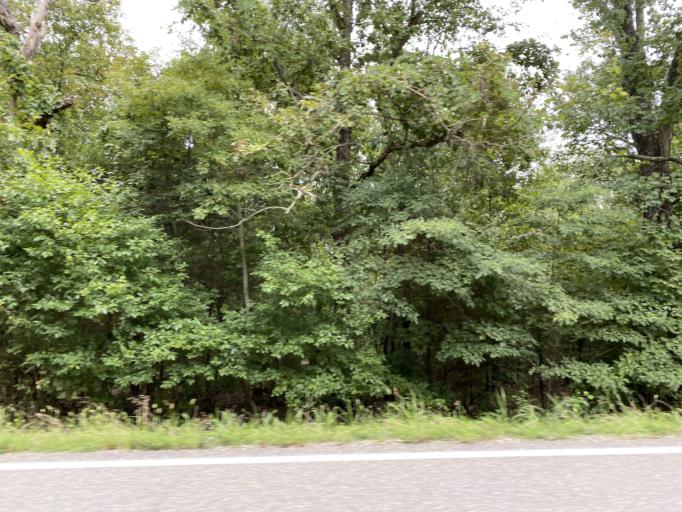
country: US
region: Arkansas
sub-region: Fulton County
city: Salem
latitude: 36.4198
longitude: -91.7169
